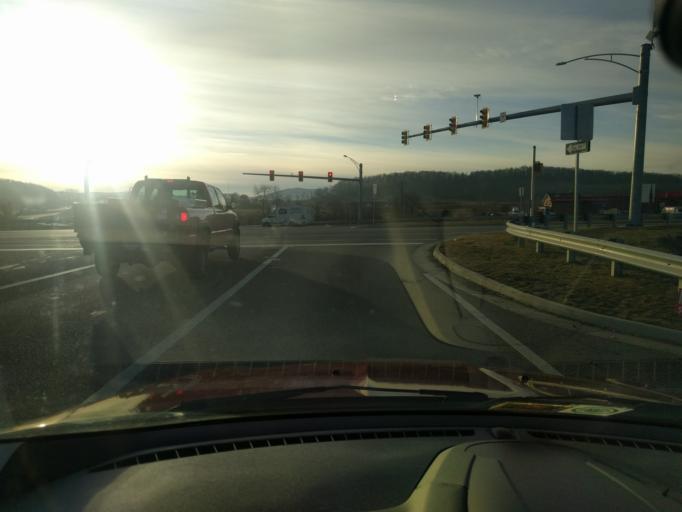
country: US
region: Virginia
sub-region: Augusta County
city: Fishersville
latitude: 38.0826
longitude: -78.9904
